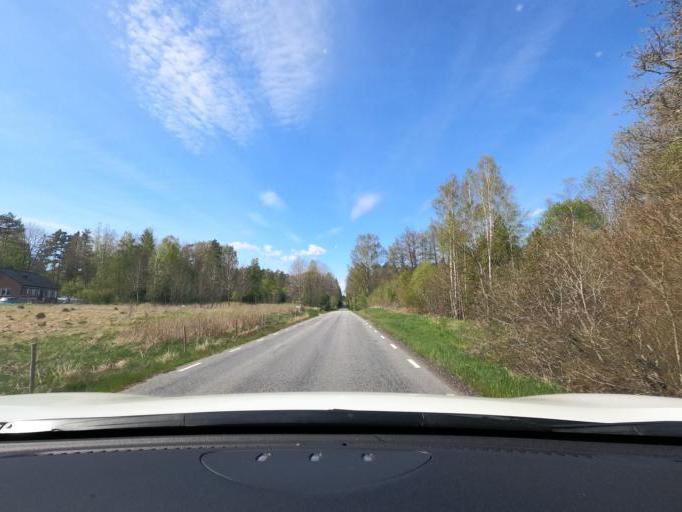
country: SE
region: Vaestra Goetaland
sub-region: Marks Kommun
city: Kinna
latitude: 57.4791
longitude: 12.5686
